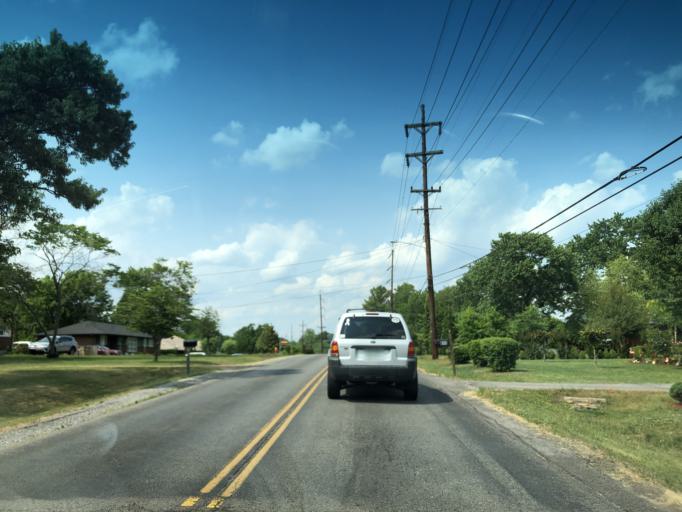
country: US
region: Tennessee
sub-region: Davidson County
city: Goodlettsville
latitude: 36.2589
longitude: -86.7190
